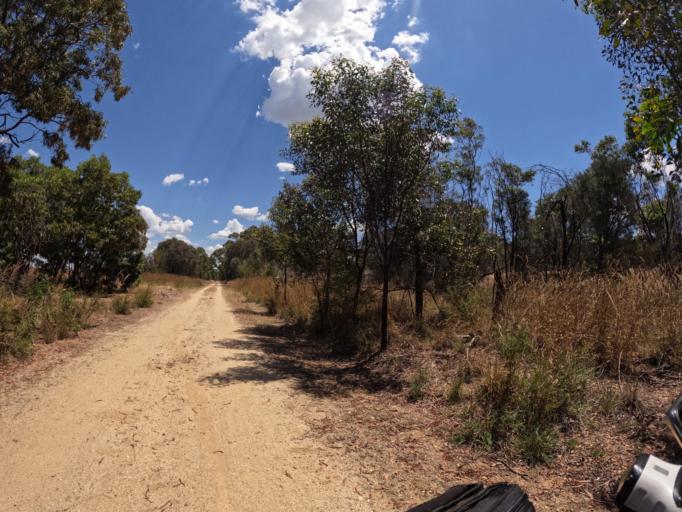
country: AU
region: Victoria
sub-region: Wellington
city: Heyfield
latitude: -37.9791
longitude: 146.8489
